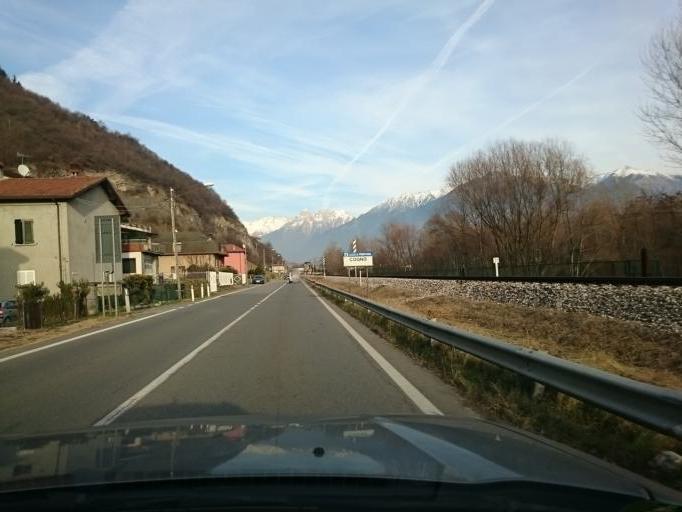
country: IT
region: Lombardy
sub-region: Provincia di Brescia
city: Piamborno
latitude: 45.9253
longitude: 10.2343
